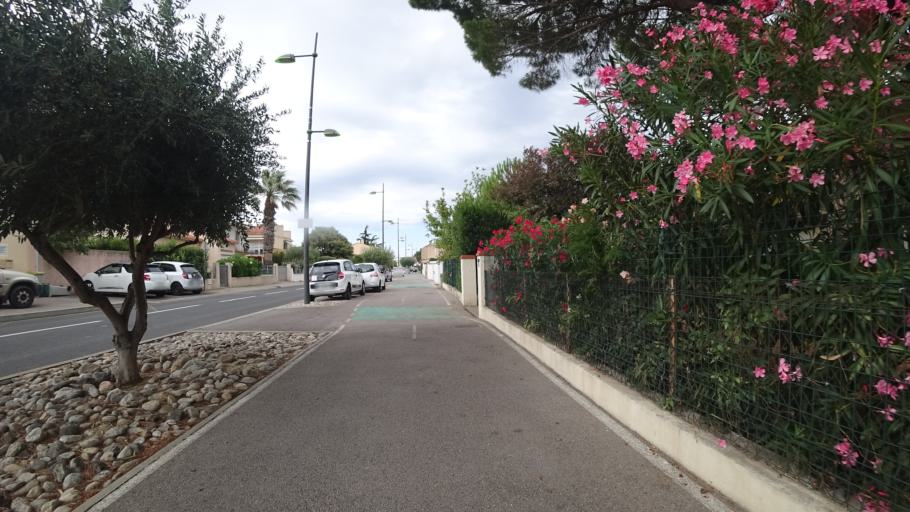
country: FR
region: Languedoc-Roussillon
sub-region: Departement des Pyrenees-Orientales
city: Saint-Laurent-de-la-Salanque
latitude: 42.7678
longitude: 2.9871
